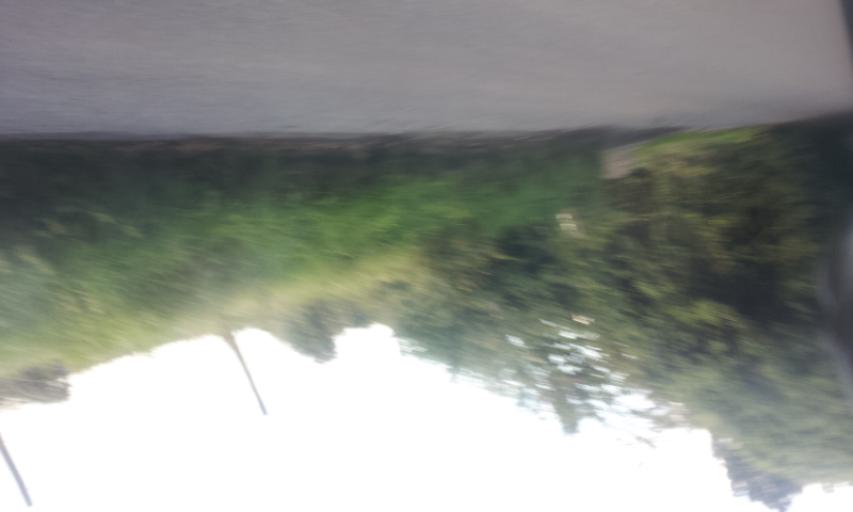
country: GB
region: England
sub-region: Kent
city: Meopham
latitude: 51.3859
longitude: 0.3846
